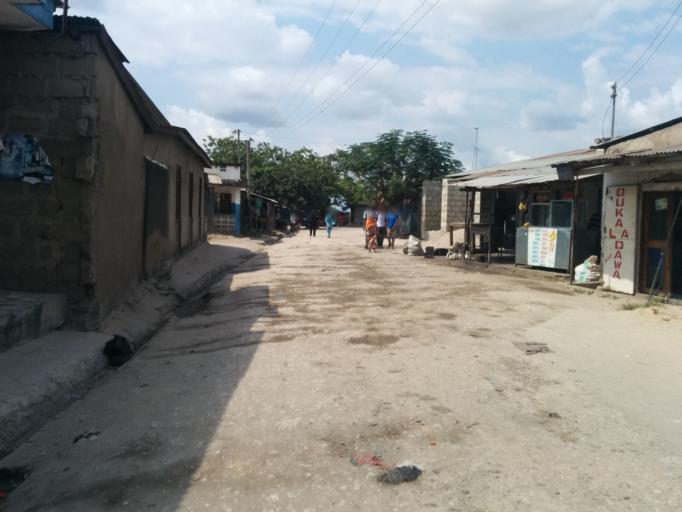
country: TZ
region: Dar es Salaam
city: Dar es Salaam
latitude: -6.8633
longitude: 39.2508
